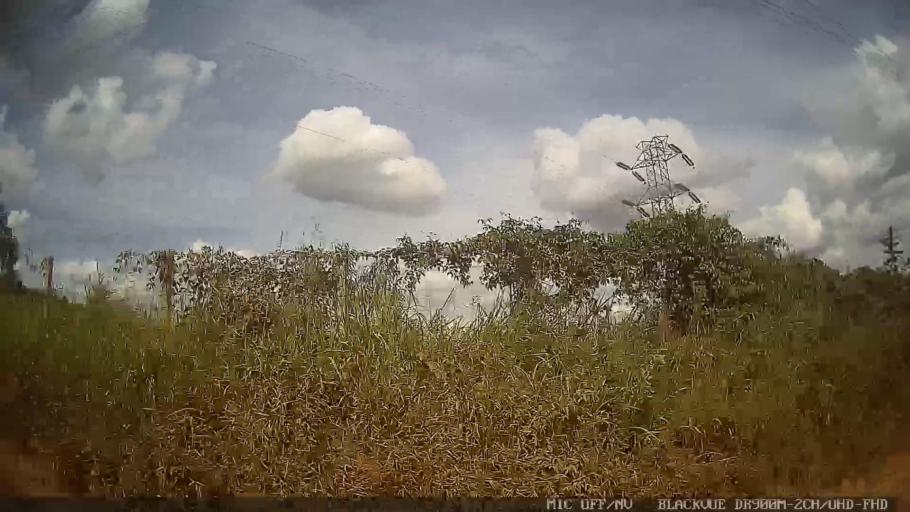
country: BR
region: Sao Paulo
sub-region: Atibaia
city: Atibaia
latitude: -23.0887
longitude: -46.5632
